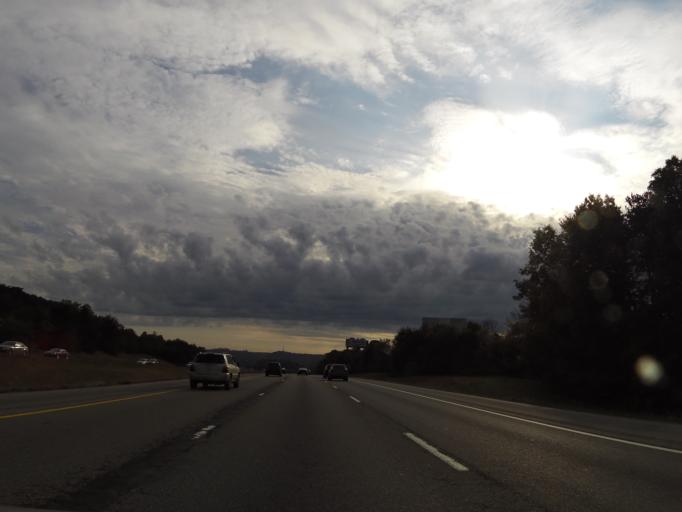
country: US
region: Tennessee
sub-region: Knox County
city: Mascot
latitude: 36.0030
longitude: -83.7840
